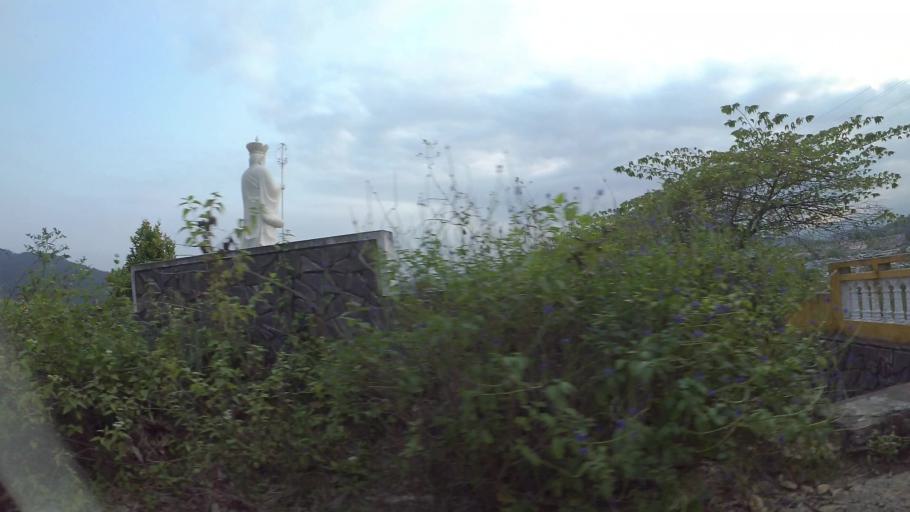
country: VN
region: Da Nang
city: Lien Chieu
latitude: 16.0628
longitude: 108.1115
